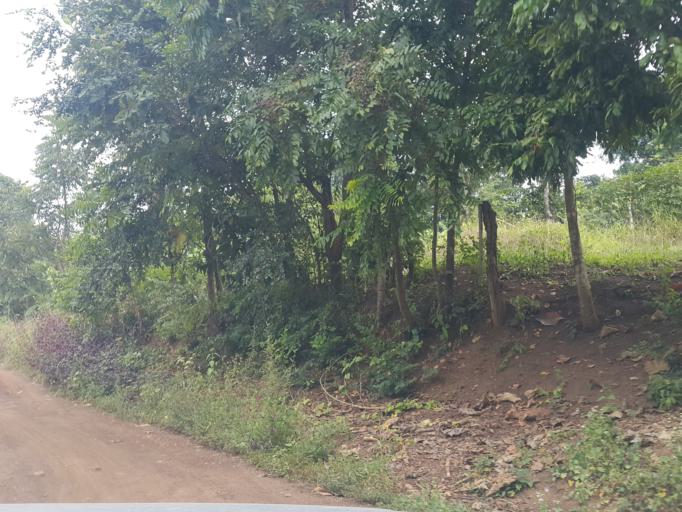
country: TH
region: Chiang Mai
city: Pai
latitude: 19.3636
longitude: 98.4507
